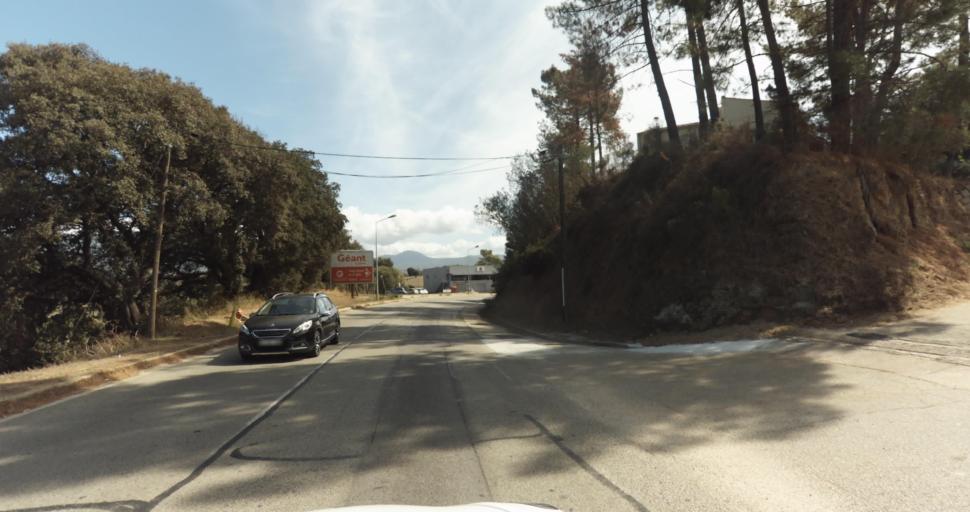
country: FR
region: Corsica
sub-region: Departement de la Corse-du-Sud
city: Afa
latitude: 41.9557
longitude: 8.7829
